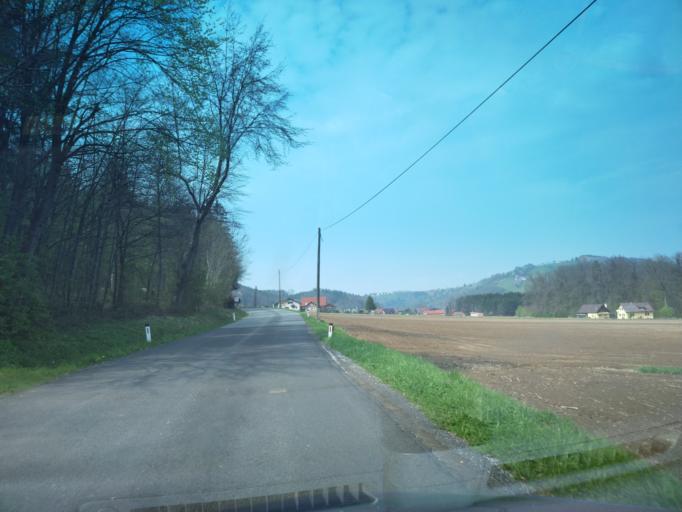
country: AT
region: Styria
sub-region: Politischer Bezirk Leibnitz
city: Grossklein
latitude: 46.7448
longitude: 15.4263
